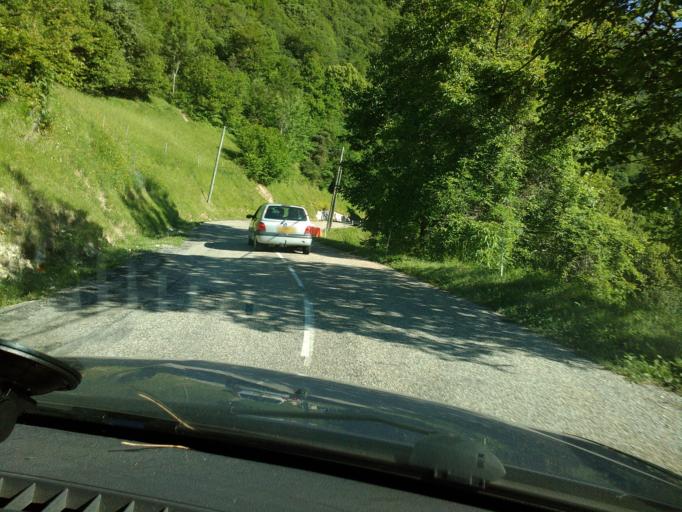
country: FR
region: Rhone-Alpes
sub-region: Departement de l'Isere
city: Saint-Egreve
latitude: 45.2745
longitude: 5.7051
